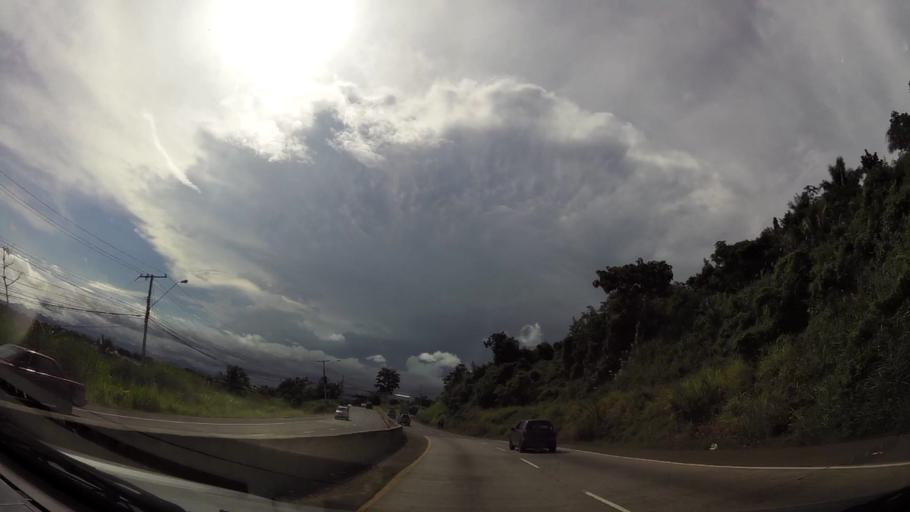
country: PA
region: Panama
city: La Chorrera
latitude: 8.8894
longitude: -79.7669
